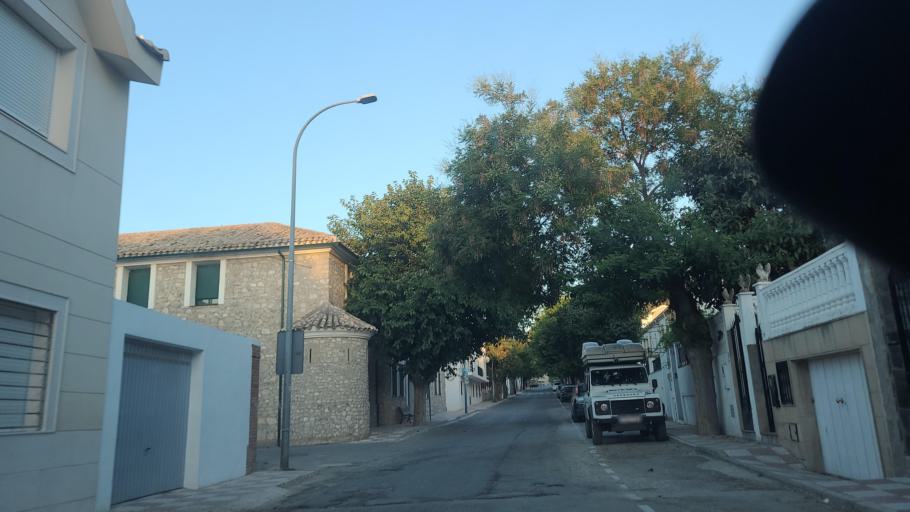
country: ES
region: Andalusia
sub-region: Provincia de Jaen
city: Jimena
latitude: 37.8433
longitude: -3.4814
